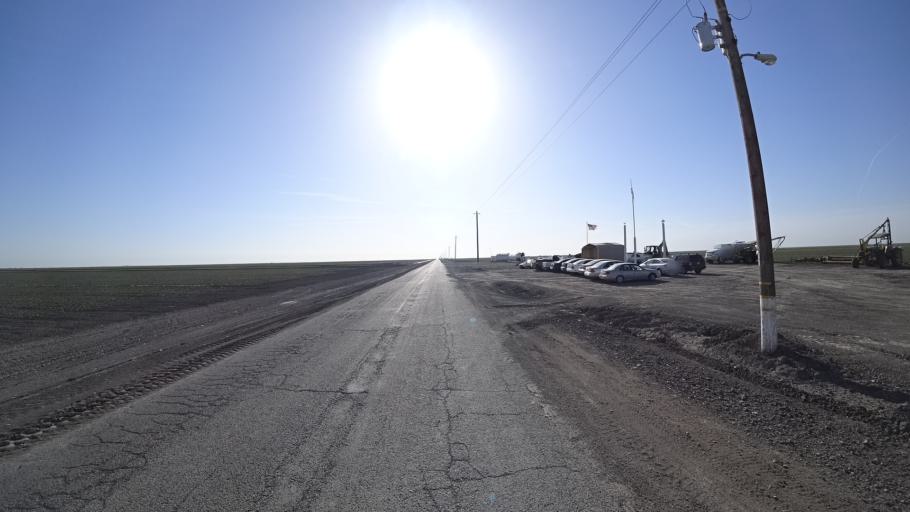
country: US
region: California
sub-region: Kings County
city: Stratford
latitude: 36.0796
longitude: -119.7908
